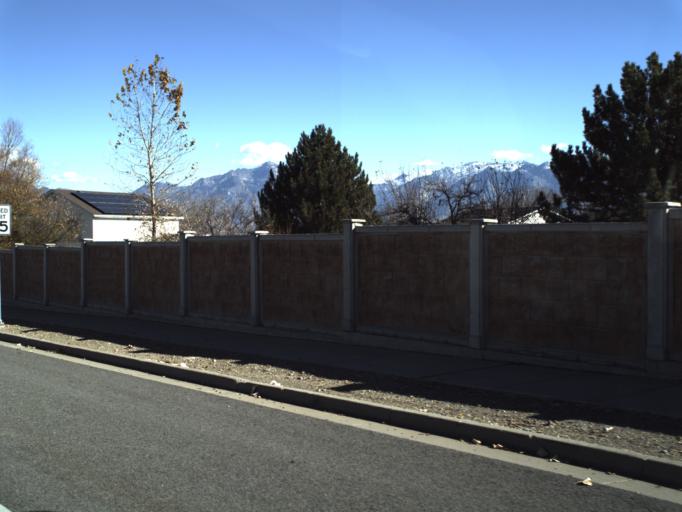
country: US
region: Utah
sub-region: Salt Lake County
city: Oquirrh
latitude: 40.5975
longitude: -112.0160
